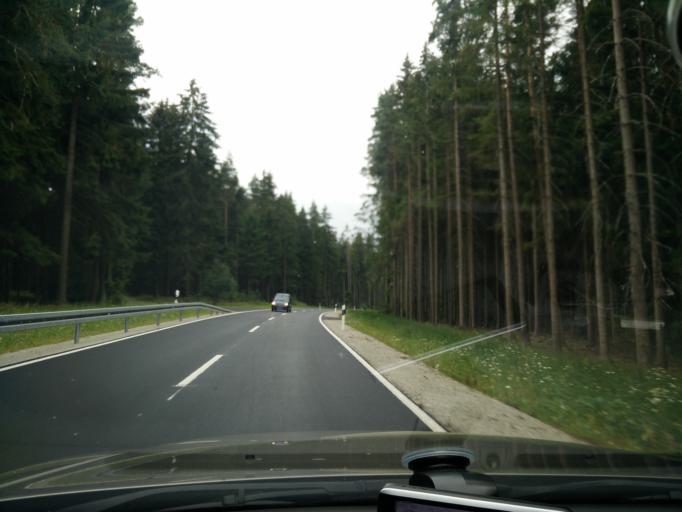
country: DE
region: Bavaria
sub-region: Upper Franconia
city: Wunsiedel
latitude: 50.0447
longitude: 11.9697
